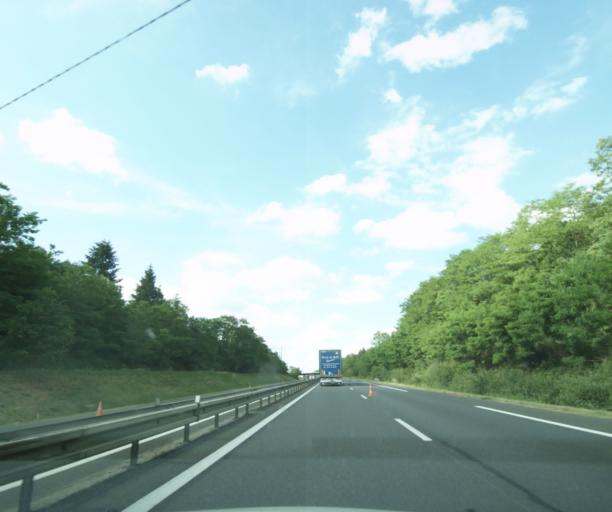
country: FR
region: Centre
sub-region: Departement du Loiret
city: La Ferte-Saint-Aubin
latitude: 47.6988
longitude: 1.9028
